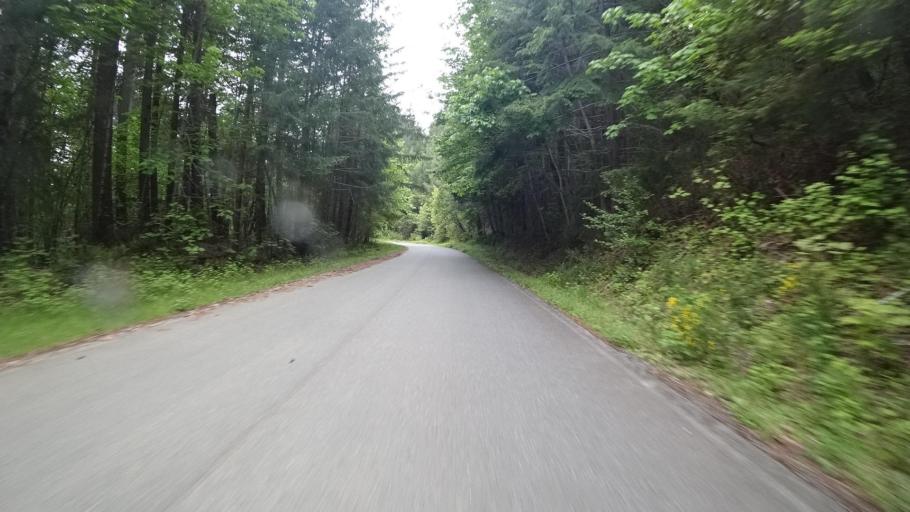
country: US
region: California
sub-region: Humboldt County
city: Willow Creek
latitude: 41.1198
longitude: -123.7375
